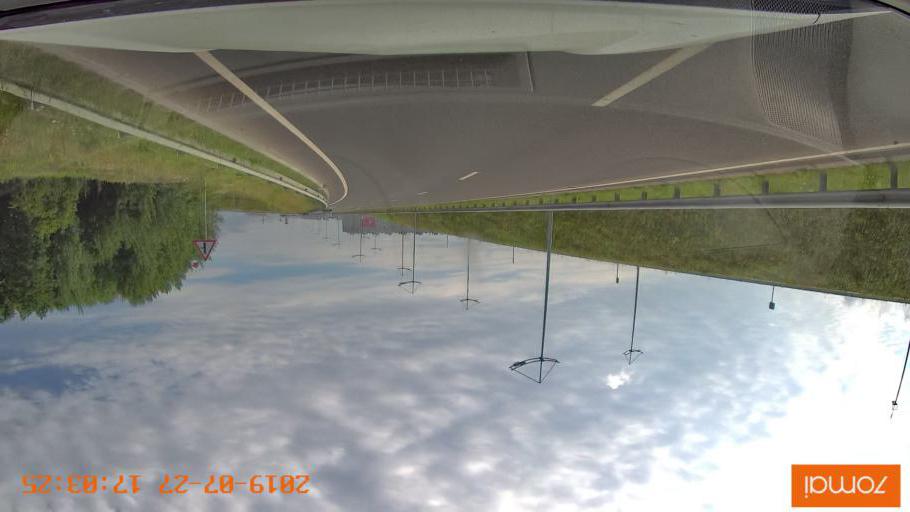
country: RU
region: Kaliningrad
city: Bol'shoe Isakovo
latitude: 54.7045
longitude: 20.6024
